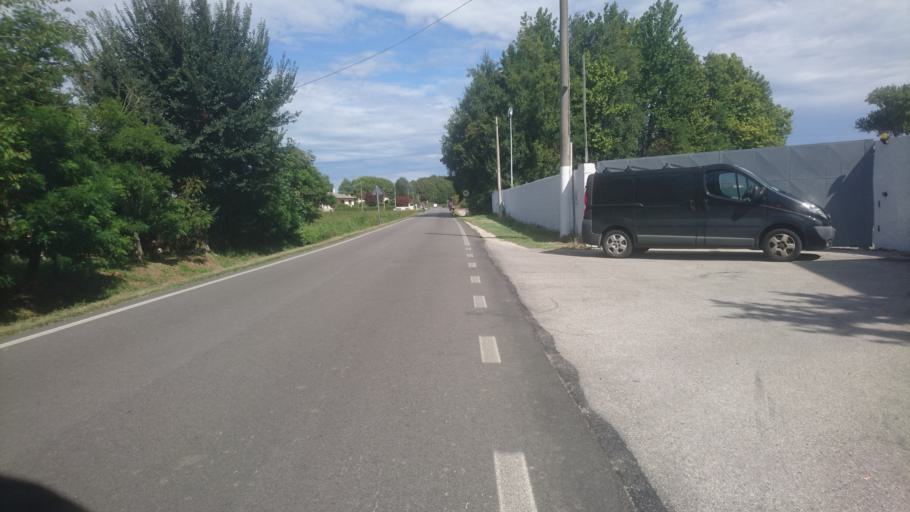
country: IT
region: Veneto
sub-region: Provincia di Venezia
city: Mira Taglio
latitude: 45.4290
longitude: 12.1567
